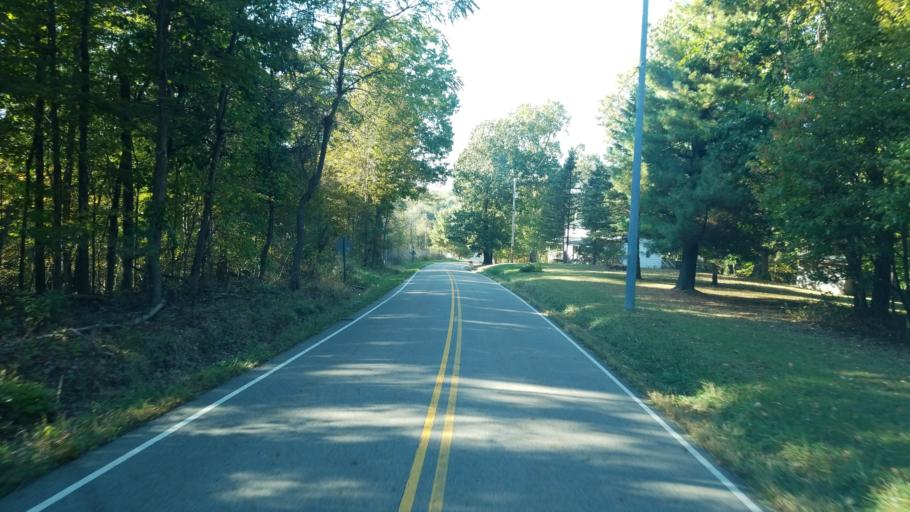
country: US
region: Ohio
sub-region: Licking County
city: Utica
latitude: 40.1696
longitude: -82.3791
